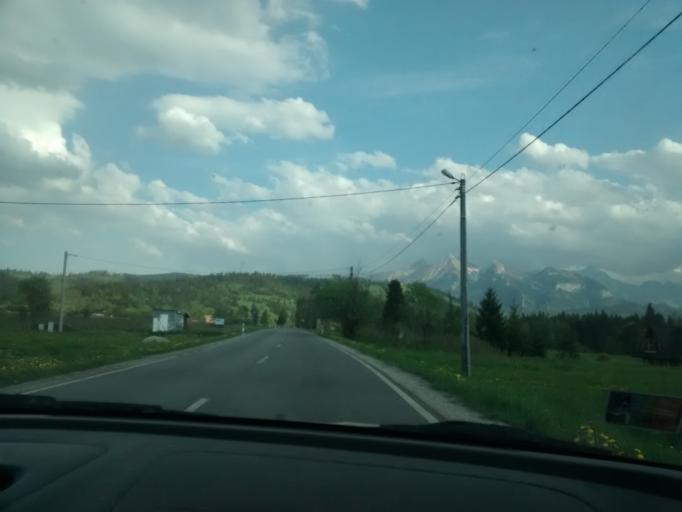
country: PL
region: Lesser Poland Voivodeship
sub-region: Powiat tatrzanski
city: Bukowina Tatrzanska
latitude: 49.3320
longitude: 20.1481
